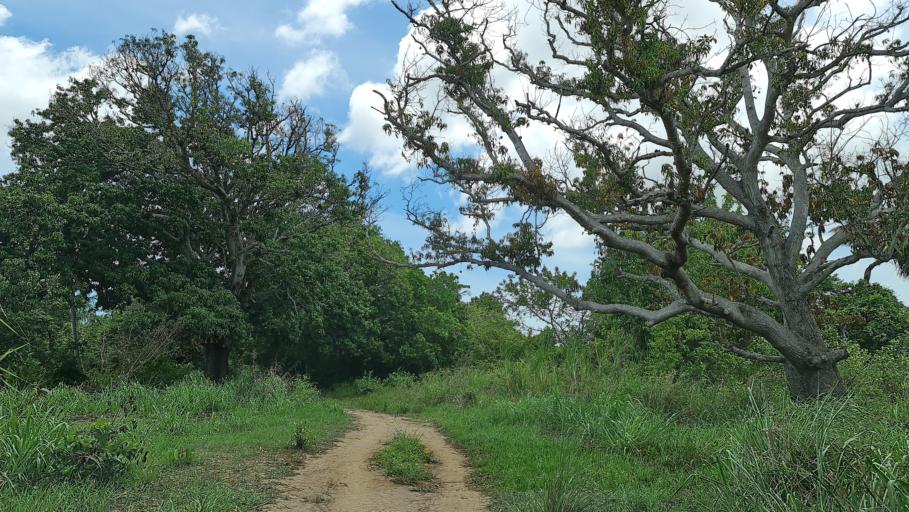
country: MZ
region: Zambezia
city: Quelimane
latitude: -17.5869
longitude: 37.3954
